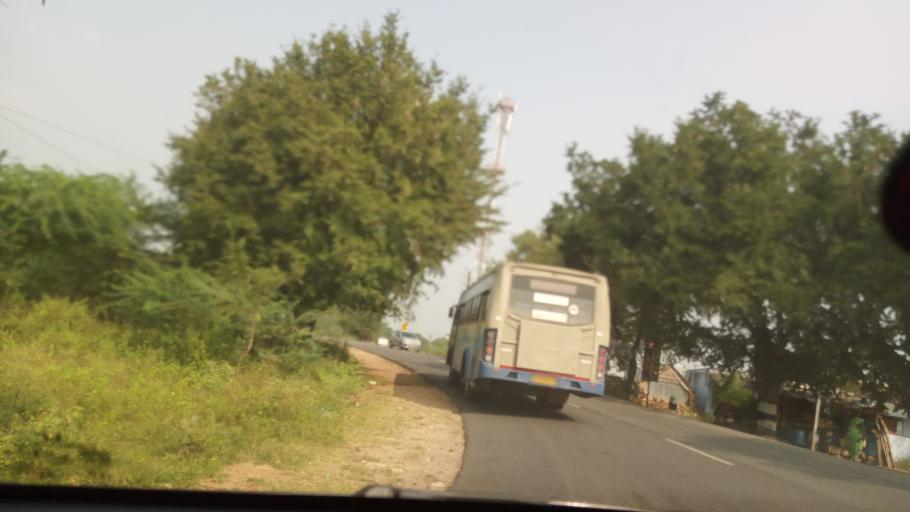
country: IN
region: Tamil Nadu
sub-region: Erode
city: Punjai Puliyampatti
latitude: 11.4198
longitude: 77.1949
